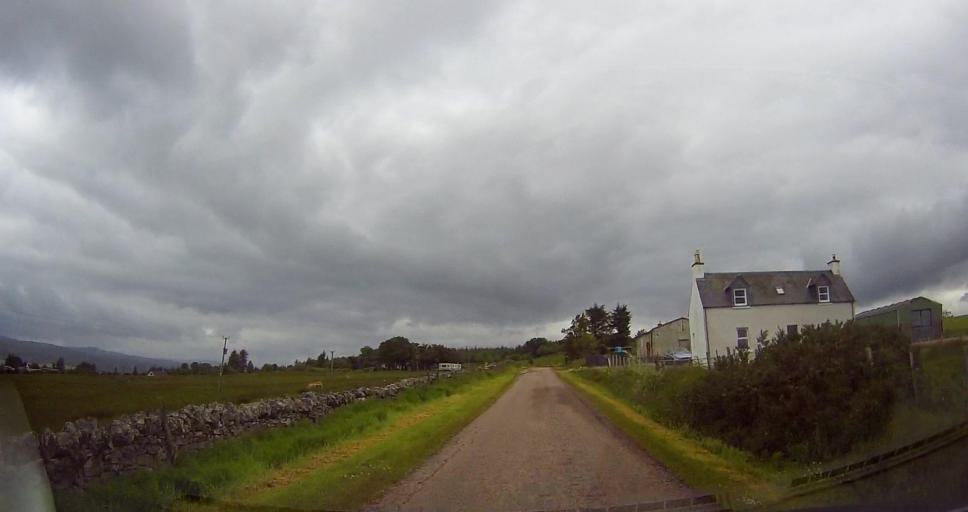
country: GB
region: Scotland
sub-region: Highland
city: Alness
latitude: 58.0788
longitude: -4.4457
